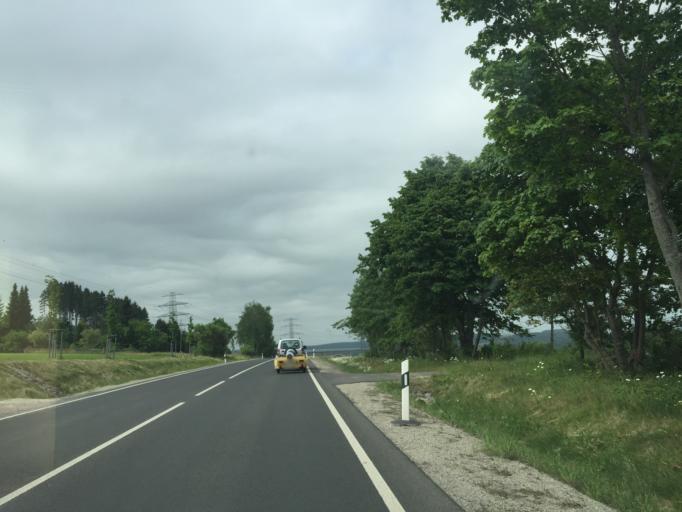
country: DE
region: Thuringia
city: Gehren
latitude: 50.6565
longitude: 10.9892
